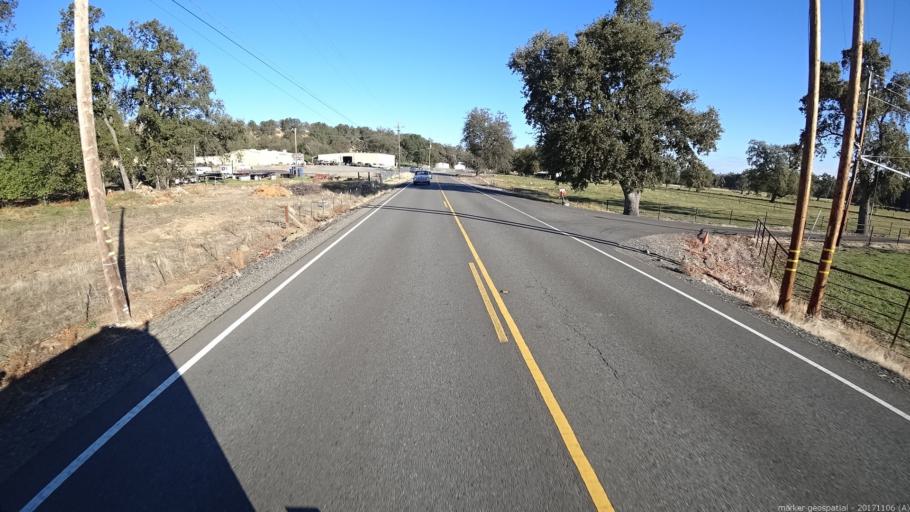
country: US
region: California
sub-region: Shasta County
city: Bella Vista
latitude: 40.6126
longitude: -122.2349
